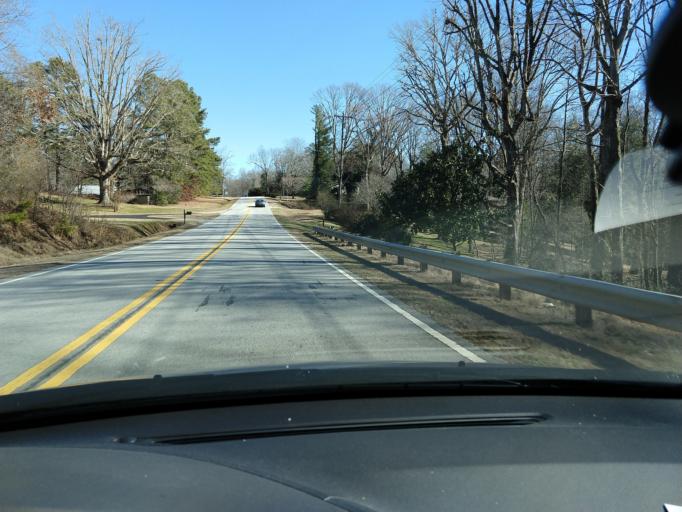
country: US
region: Georgia
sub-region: Stephens County
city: Toccoa
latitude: 34.6151
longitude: -83.4079
